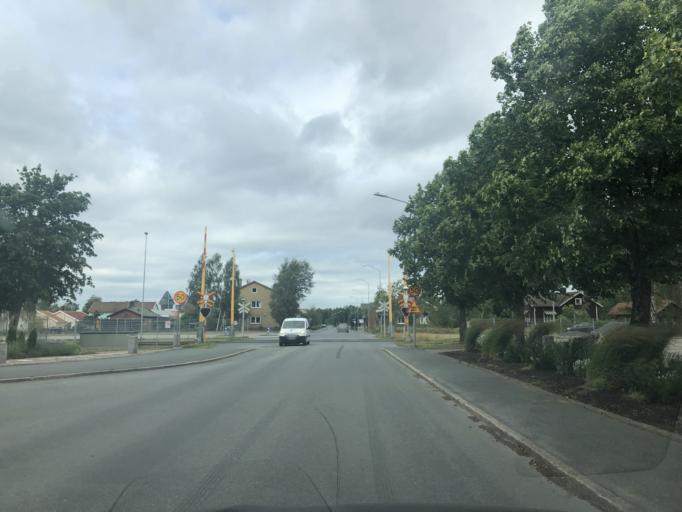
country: SE
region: Joenkoeping
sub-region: Vaggeryds Kommun
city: Vaggeryd
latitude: 57.4992
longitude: 14.1486
